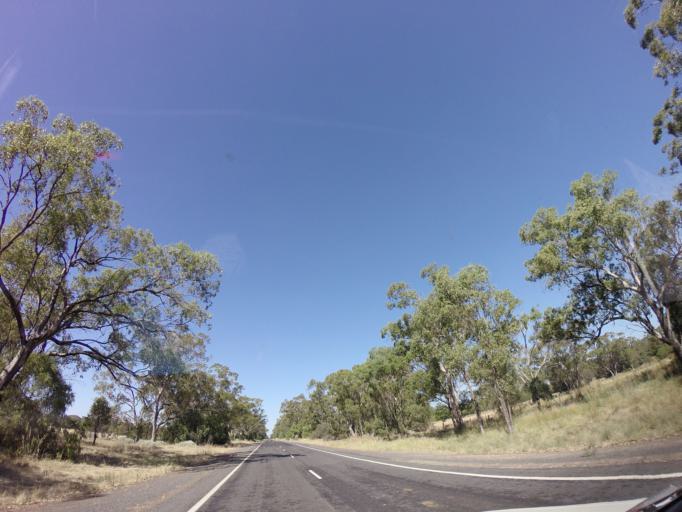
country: AU
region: New South Wales
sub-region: Narromine
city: Narromine
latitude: -31.6568
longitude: 147.8755
